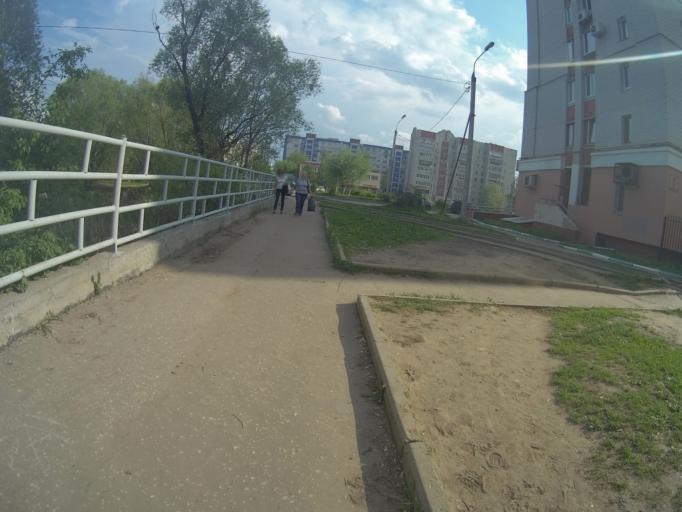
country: RU
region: Vladimir
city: Kommunar
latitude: 56.1660
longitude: 40.4509
